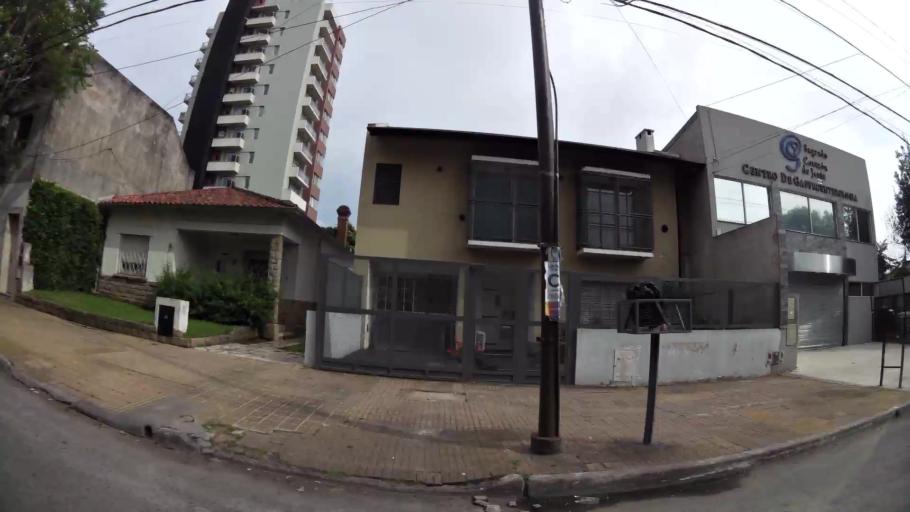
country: AR
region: Buenos Aires
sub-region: Partido de Quilmes
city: Quilmes
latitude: -34.7246
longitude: -58.2498
